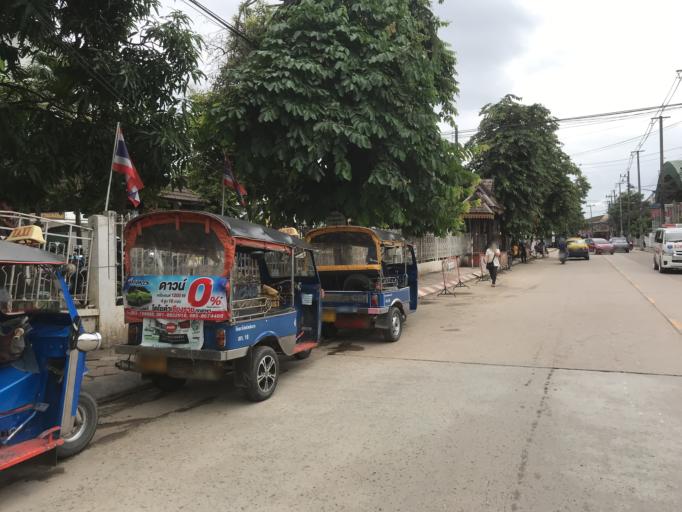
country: TH
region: Chiang Rai
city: Chiang Rai
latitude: 19.9016
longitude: 99.8300
